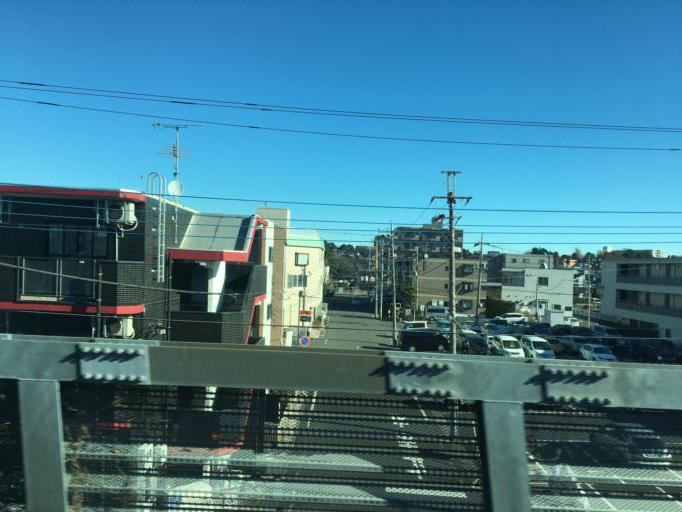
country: JP
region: Chiba
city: Nagareyama
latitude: 35.8403
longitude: 139.9021
